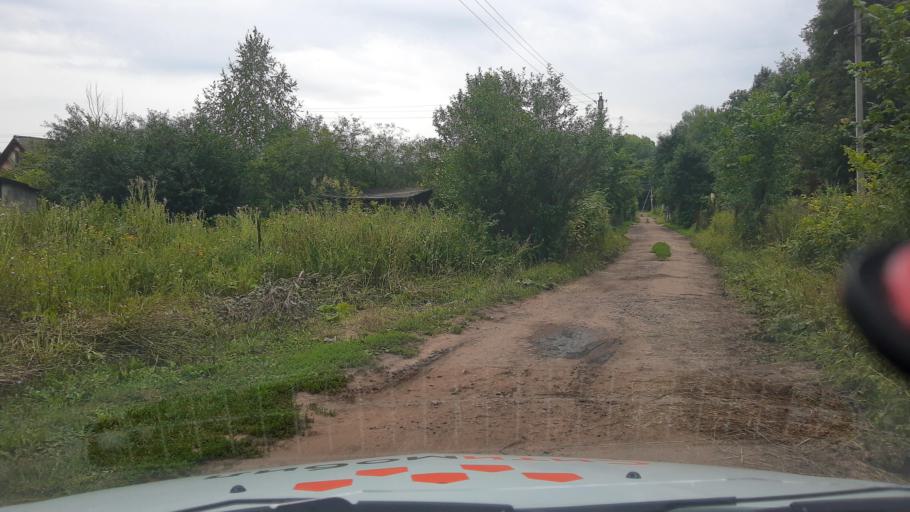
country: RU
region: Bashkortostan
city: Kabakovo
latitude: 54.6694
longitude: 56.0934
